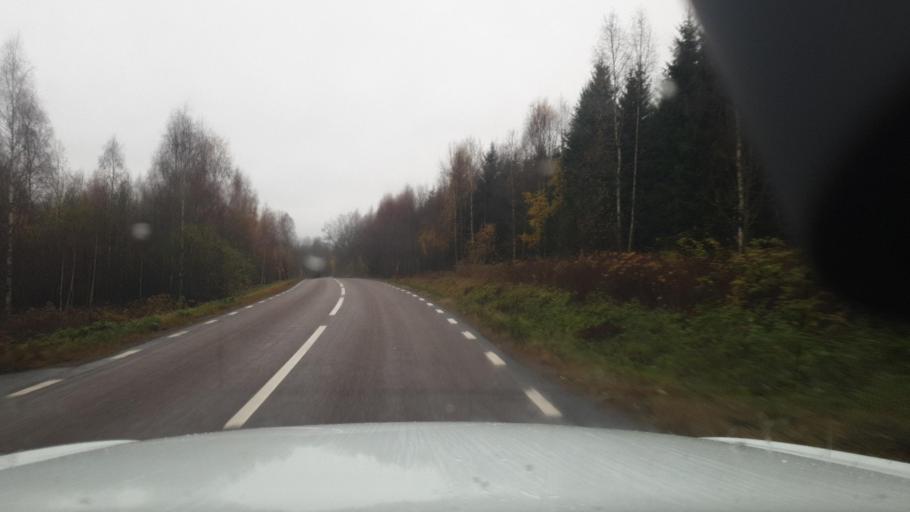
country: SE
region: Vaermland
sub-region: Torsby Kommun
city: Torsby
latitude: 59.9173
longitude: 12.8982
